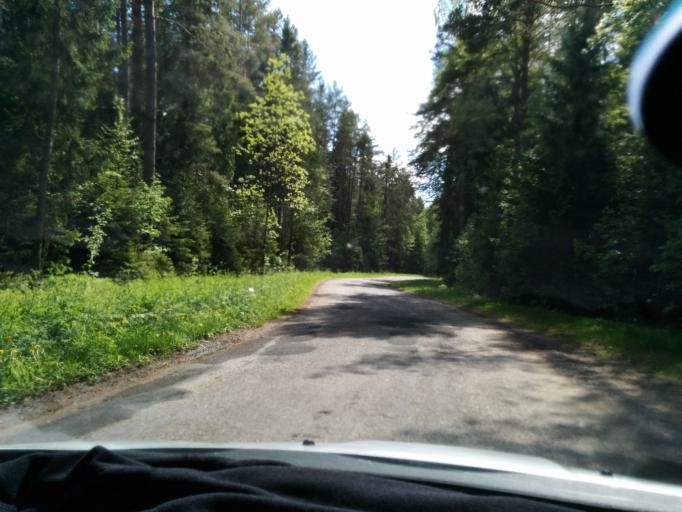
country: EE
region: Harju
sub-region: Loksa linn
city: Loksa
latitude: 59.5716
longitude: 25.7085
